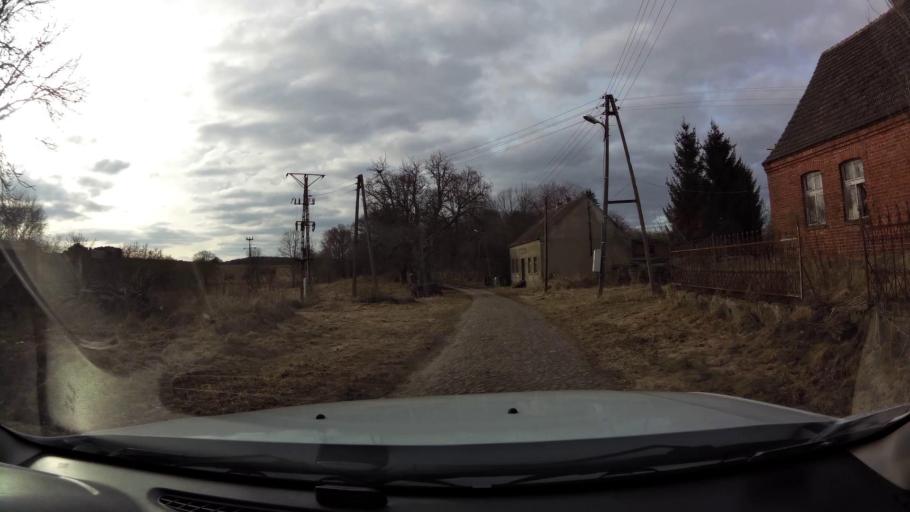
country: PL
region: West Pomeranian Voivodeship
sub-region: Powiat drawski
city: Drawsko Pomorskie
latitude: 53.5205
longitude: 15.7076
